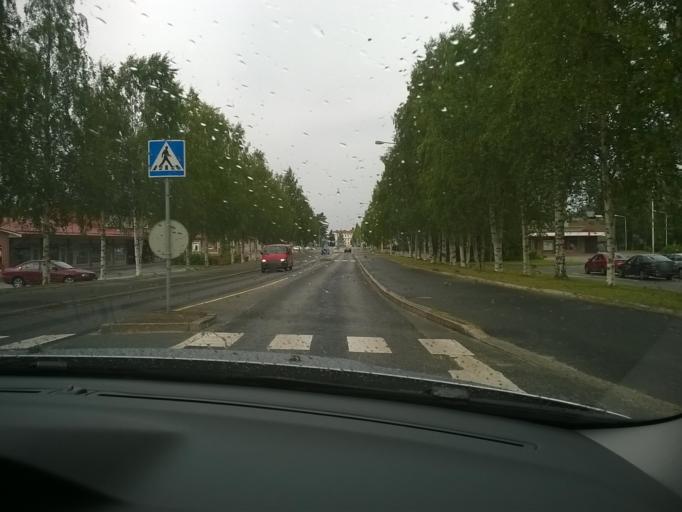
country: FI
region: Kainuu
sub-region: Kehys-Kainuu
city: Kuhmo
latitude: 64.1261
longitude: 29.5272
